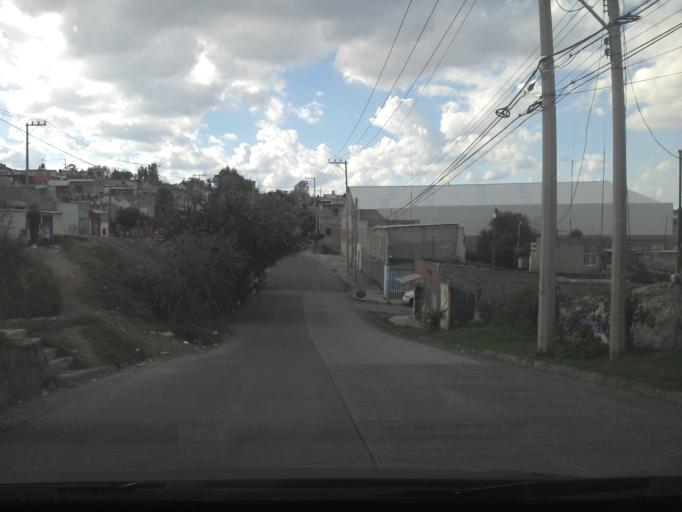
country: MX
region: Jalisco
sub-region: Tlajomulco de Zuniga
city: Altus Bosques
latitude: 20.6159
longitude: -103.3681
